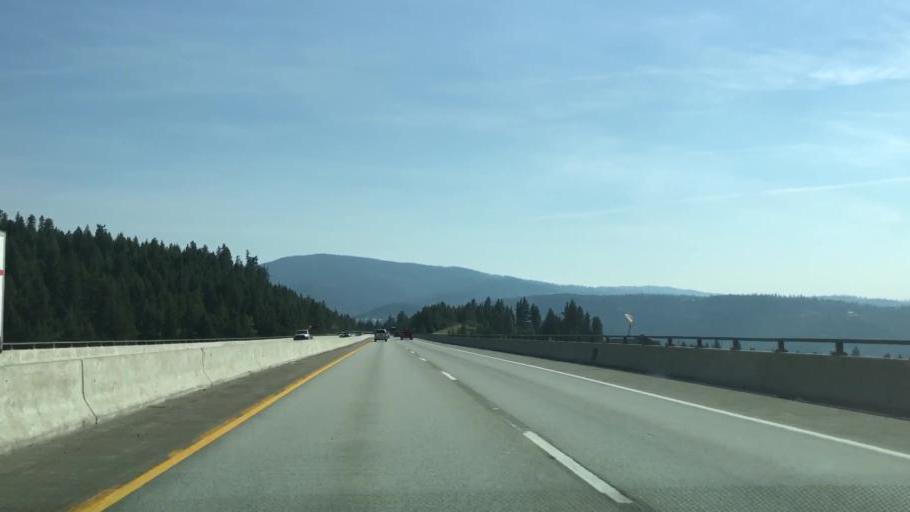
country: US
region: Idaho
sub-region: Kootenai County
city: Coeur d'Alene
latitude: 47.6481
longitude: -116.7148
